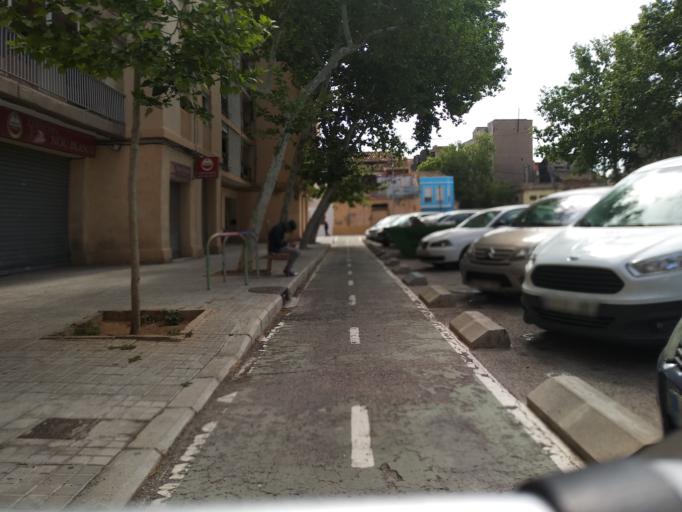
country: ES
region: Valencia
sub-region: Provincia de Valencia
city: Alboraya
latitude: 39.4706
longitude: -0.3325
